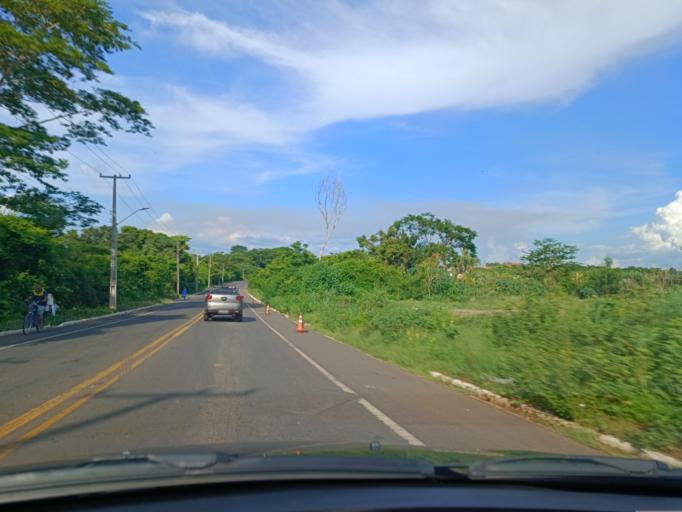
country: BR
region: Piaui
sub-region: Teresina
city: Teresina
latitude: -5.0861
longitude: -42.7567
